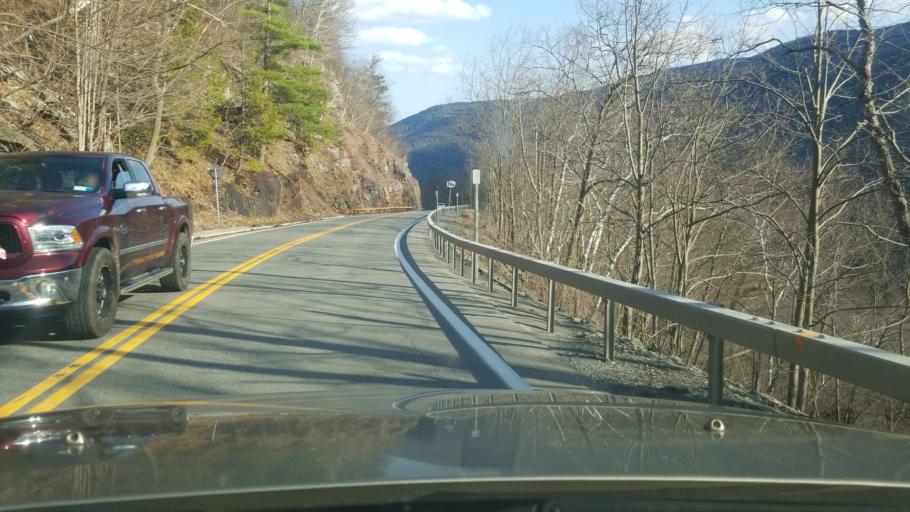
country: US
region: New York
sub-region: Greene County
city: Palenville
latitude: 42.1926
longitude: -74.0787
